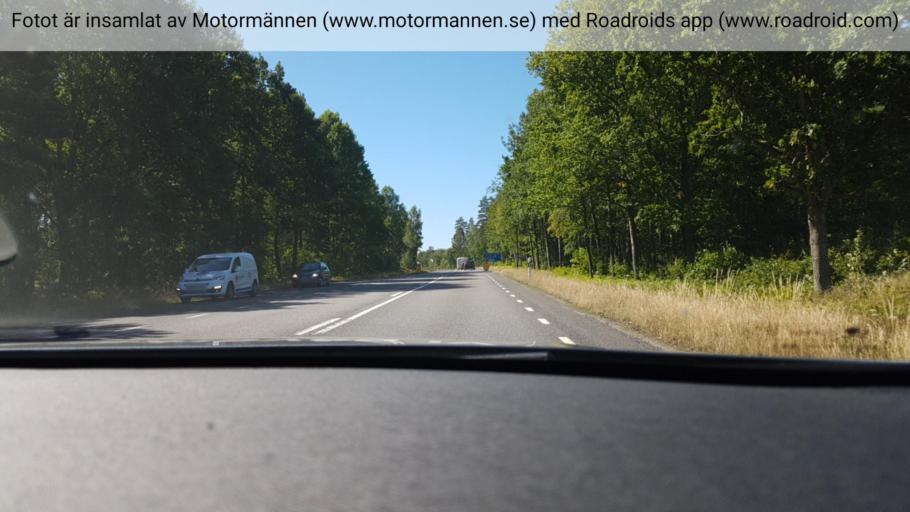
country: SE
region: Joenkoeping
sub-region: Habo Kommun
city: Habo
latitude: 57.9270
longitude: 14.0951
